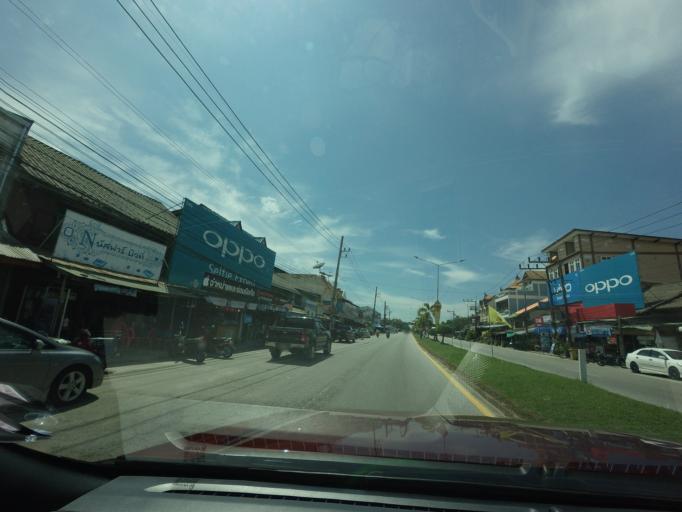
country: TH
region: Pattani
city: Mai Kaen
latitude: 6.6107
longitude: 101.6301
